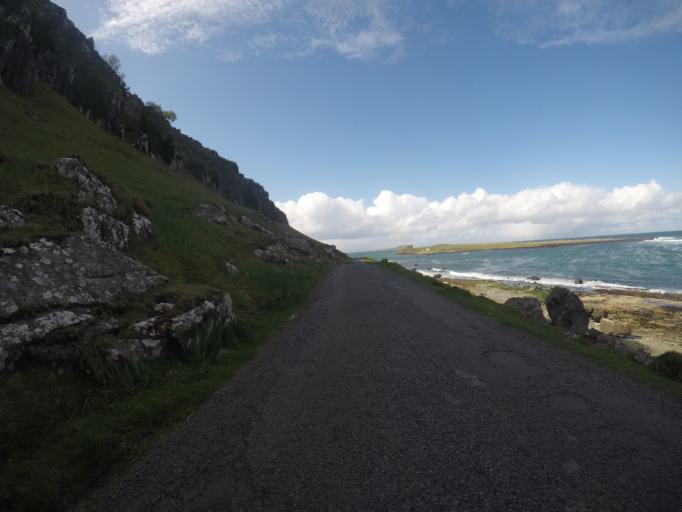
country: GB
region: Scotland
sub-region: Highland
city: Portree
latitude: 57.6348
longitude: -6.2029
